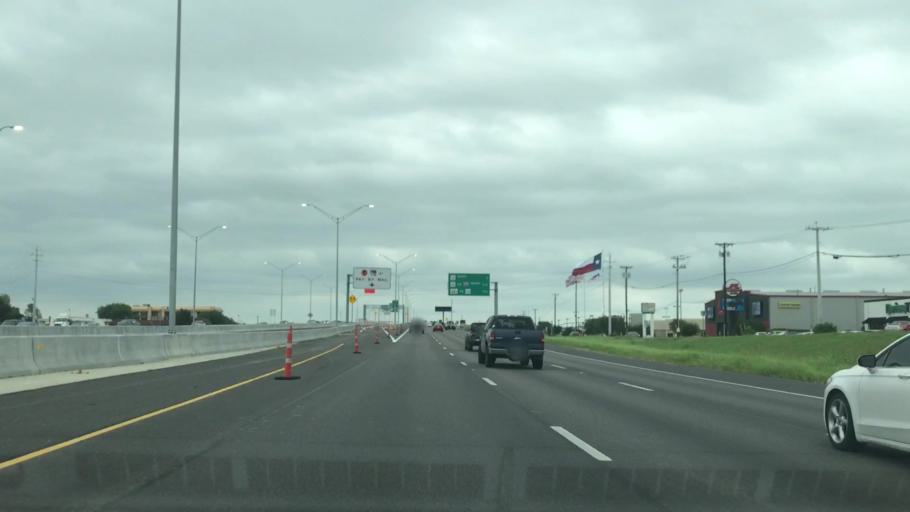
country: US
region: Texas
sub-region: Dallas County
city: Irving
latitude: 32.8370
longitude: -96.9450
